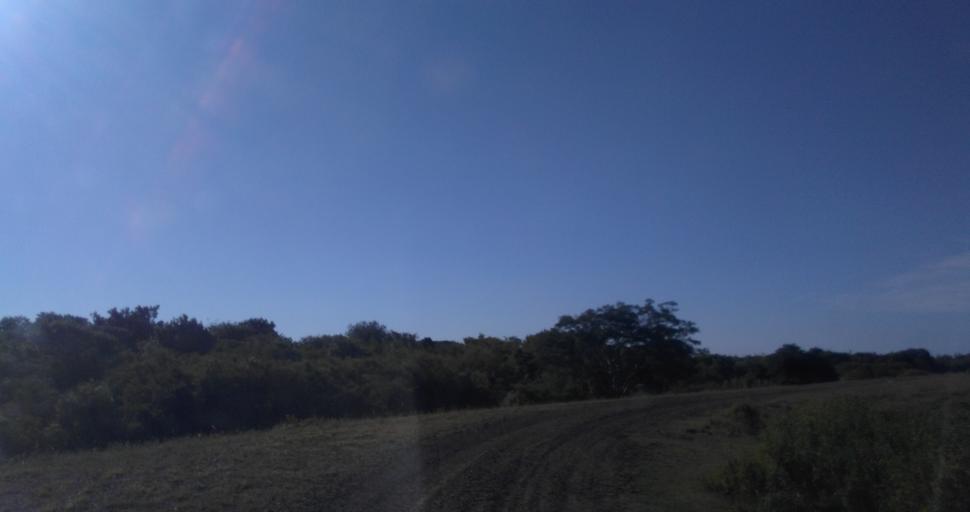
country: AR
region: Chaco
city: Barranqueras
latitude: -27.4317
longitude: -58.9246
